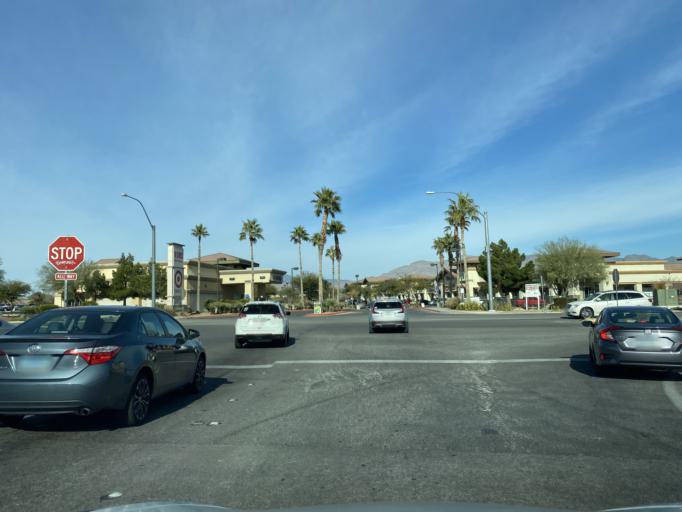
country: US
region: Nevada
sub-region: Clark County
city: Las Vegas
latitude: 36.2783
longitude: -115.2624
